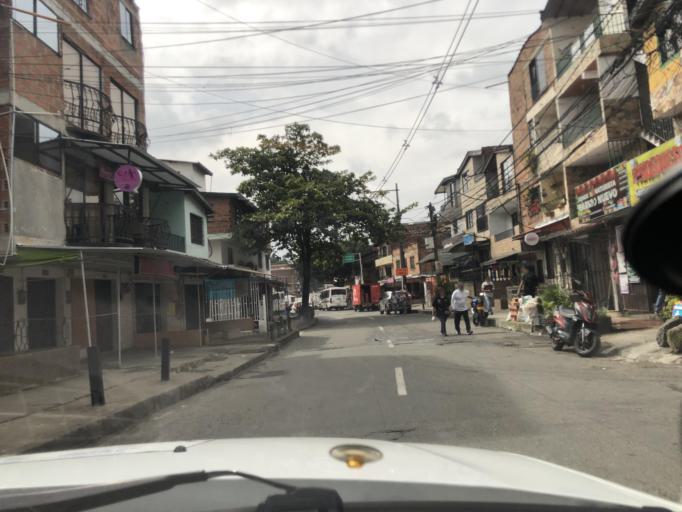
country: CO
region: Antioquia
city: Bello
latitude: 6.3132
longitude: -75.5701
